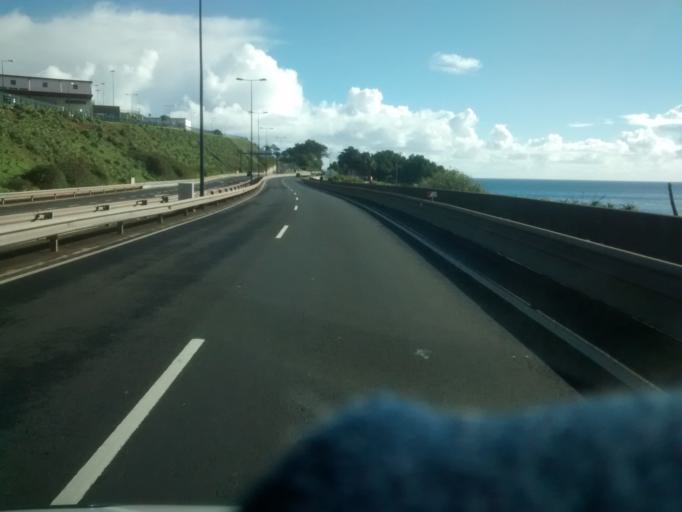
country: PT
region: Madeira
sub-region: Machico
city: Machico
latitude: 32.6895
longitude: -16.7814
